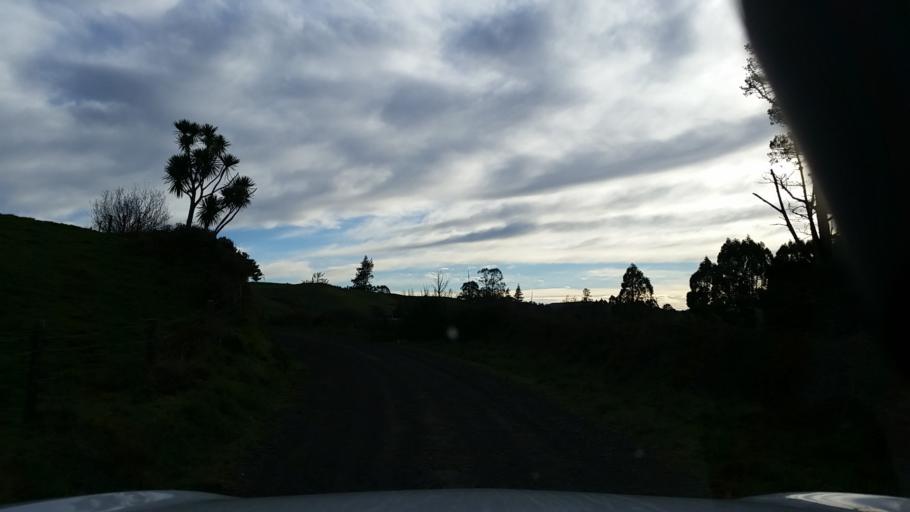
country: NZ
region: Bay of Plenty
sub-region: Rotorua District
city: Rotorua
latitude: -38.2680
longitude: 176.1569
